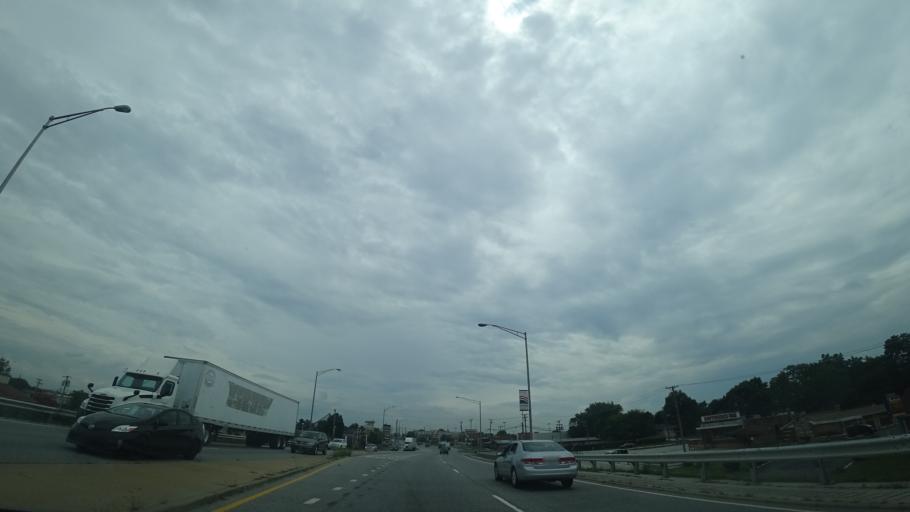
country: US
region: Illinois
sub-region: Cook County
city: Alsip
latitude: 41.6773
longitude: -87.7388
